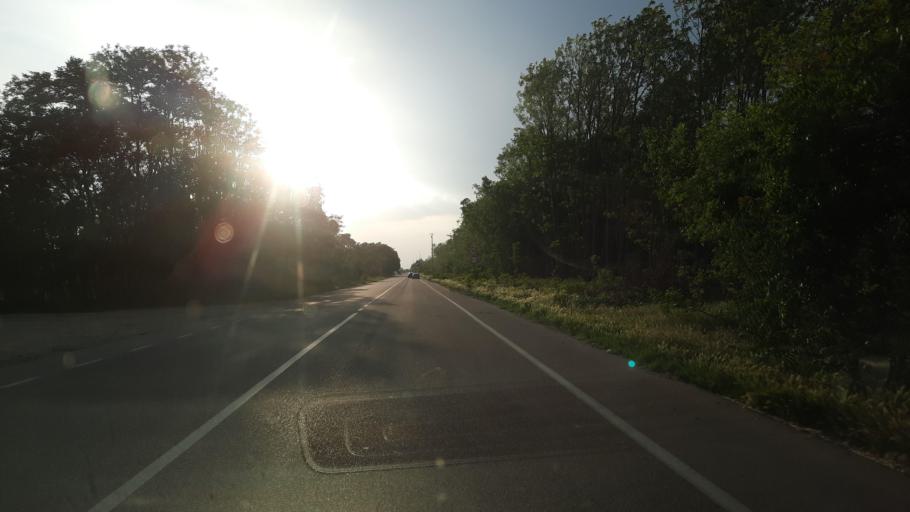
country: IT
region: Lombardy
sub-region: Provincia di Pavia
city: Cergnago
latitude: 45.2326
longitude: 8.8068
